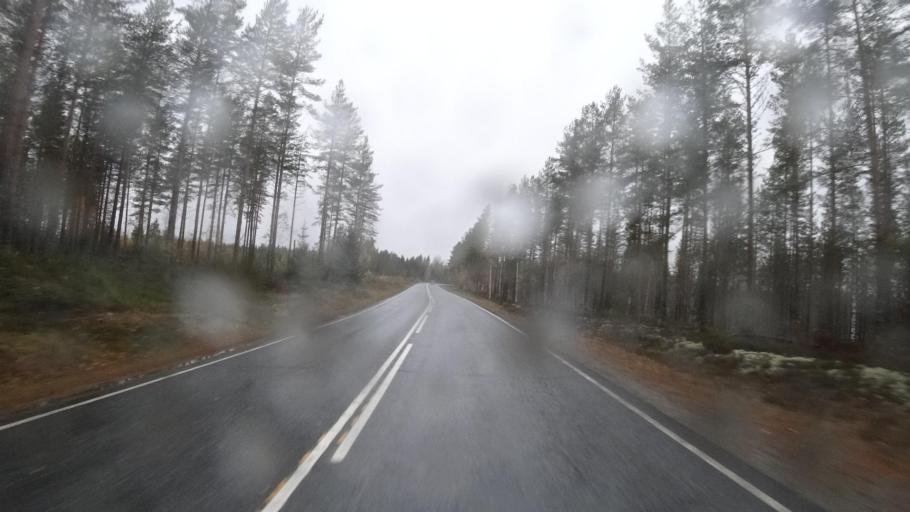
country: FI
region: Northern Savo
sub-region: Koillis-Savo
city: Tuusniemi
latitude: 62.8672
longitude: 28.4271
